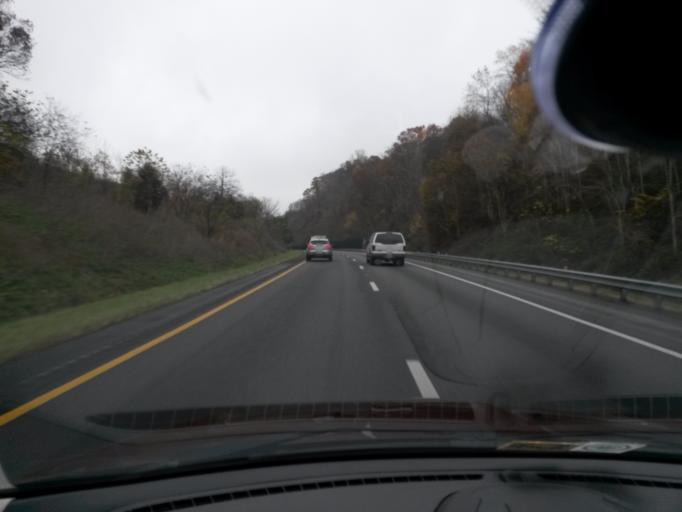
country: US
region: Virginia
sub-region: Montgomery County
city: Shawsville
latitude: 37.1850
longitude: -80.2855
